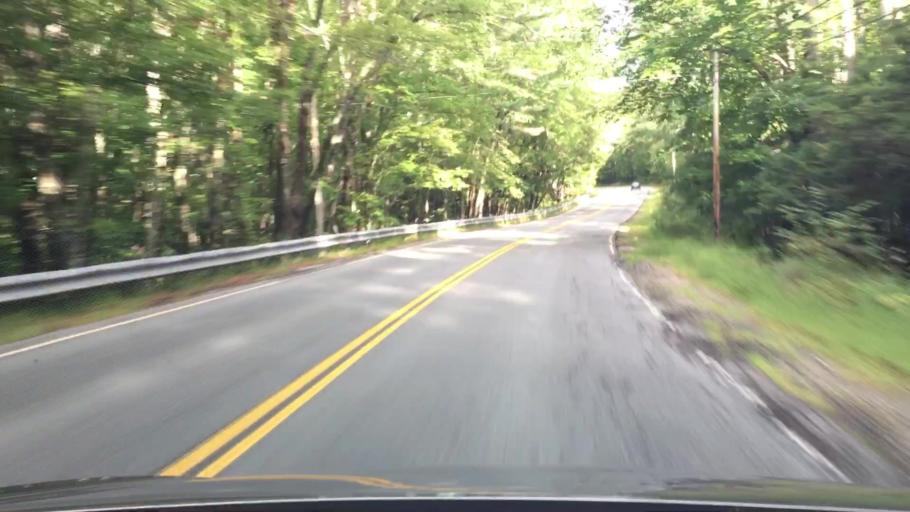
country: US
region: Maine
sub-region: Oxford County
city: Fryeburg
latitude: 44.0298
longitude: -70.9142
